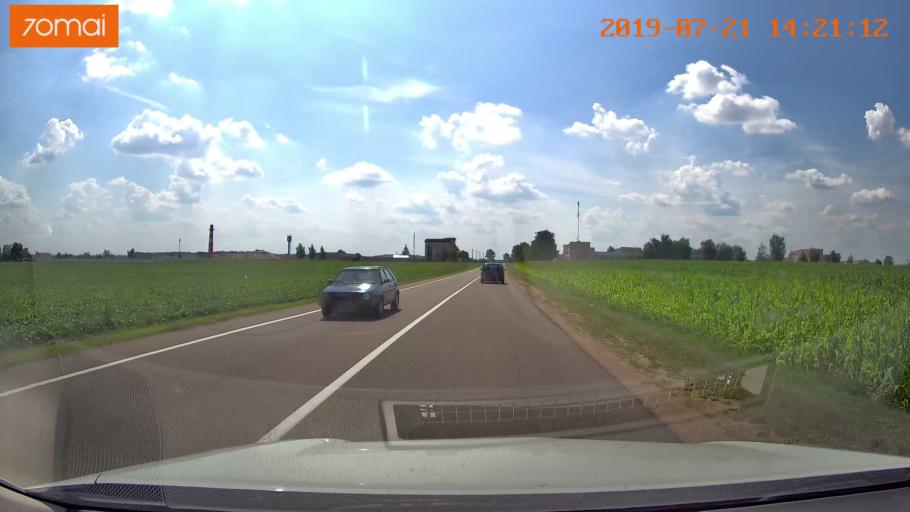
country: BY
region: Grodnenskaya
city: Karelichy
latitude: 53.5779
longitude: 26.1477
